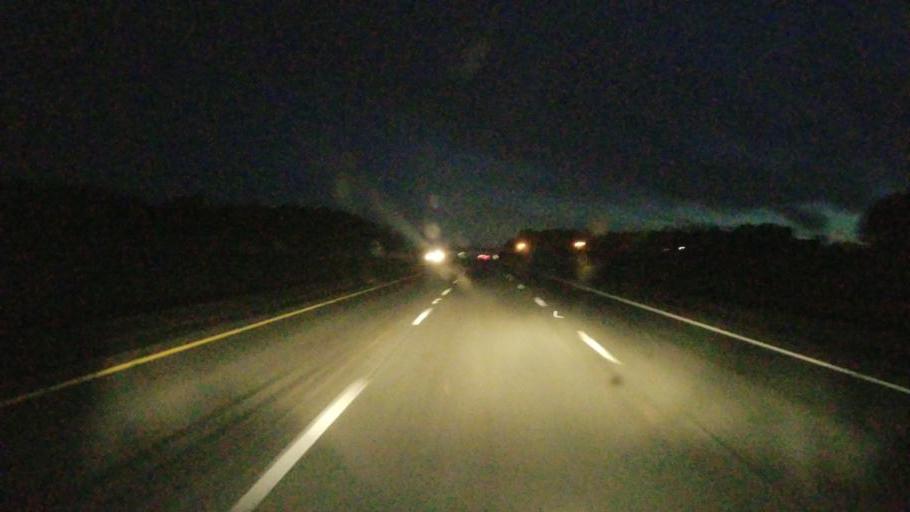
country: US
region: Ohio
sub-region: Ashland County
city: Ashland
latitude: 40.8386
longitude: -82.2933
